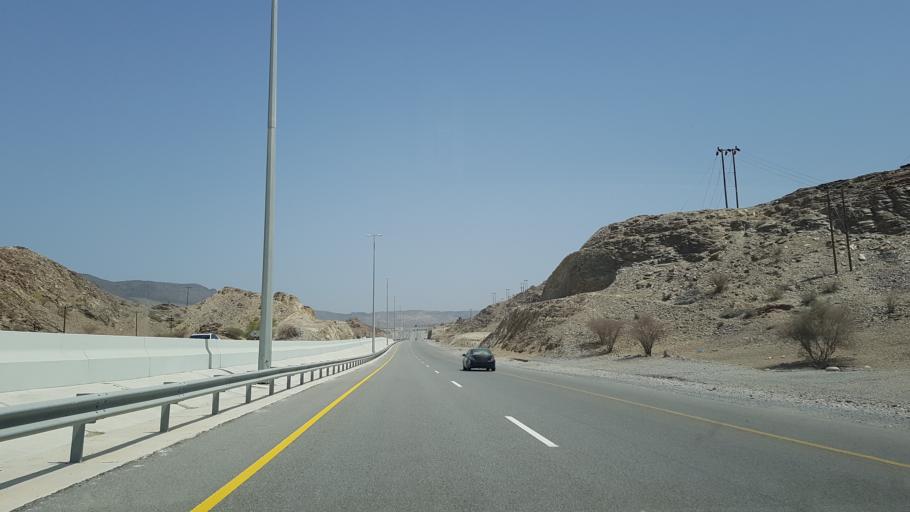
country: OM
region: Muhafazat Masqat
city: Muscat
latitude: 23.2548
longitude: 58.7772
